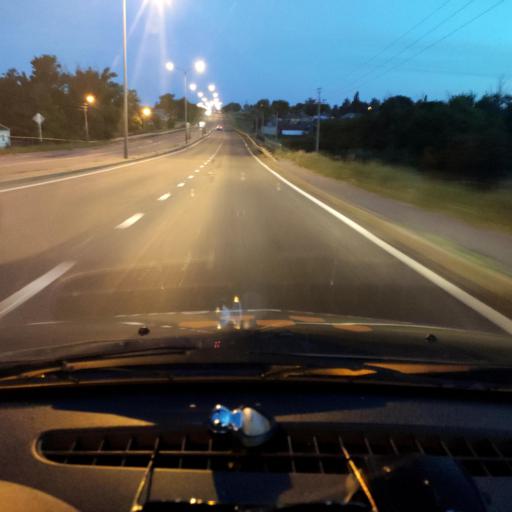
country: RU
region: Belgorod
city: Gubkin
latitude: 51.2589
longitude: 37.5300
